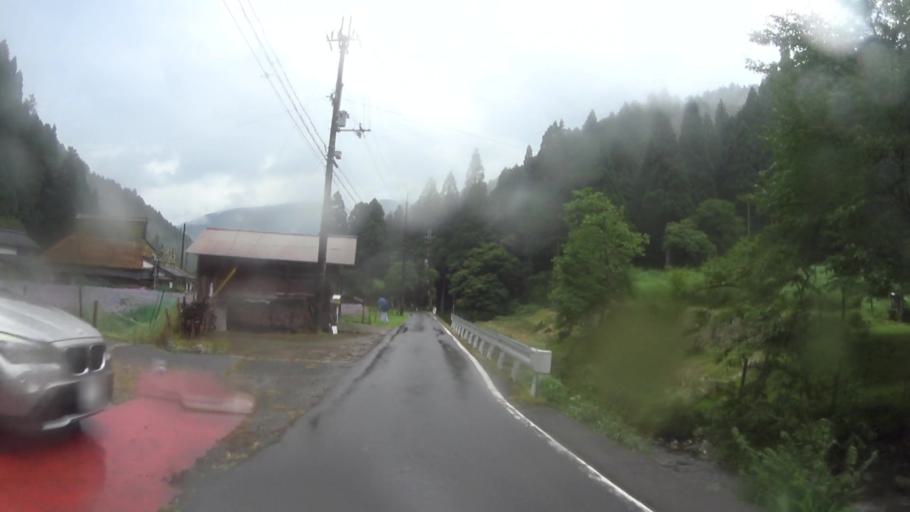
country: JP
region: Shiga Prefecture
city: Kitahama
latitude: 35.2644
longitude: 135.8088
